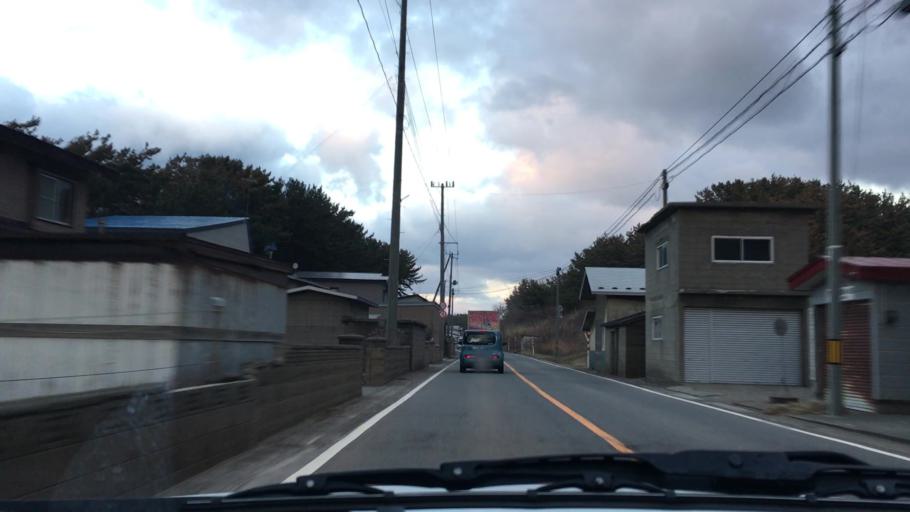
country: JP
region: Aomori
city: Shimokizukuri
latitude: 40.7555
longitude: 140.1518
